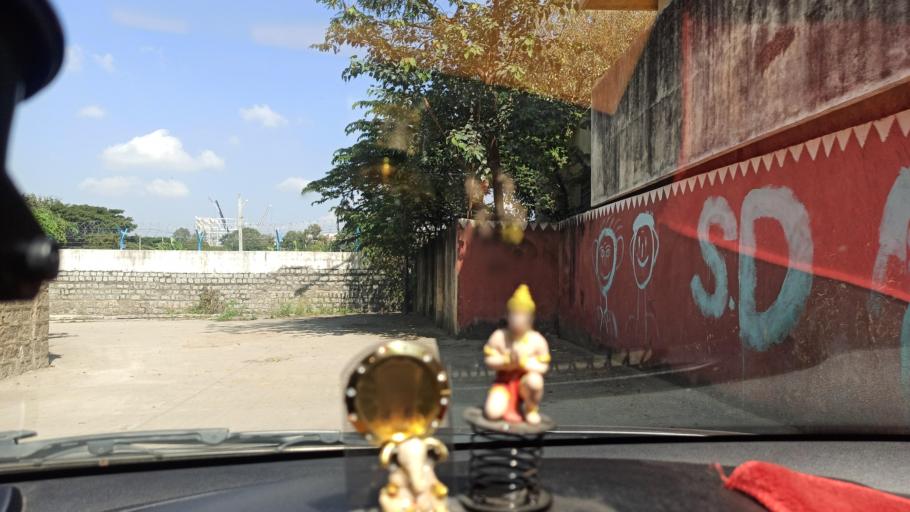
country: IN
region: Karnataka
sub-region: Bangalore Urban
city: Bangalore
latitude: 12.9586
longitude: 77.6961
